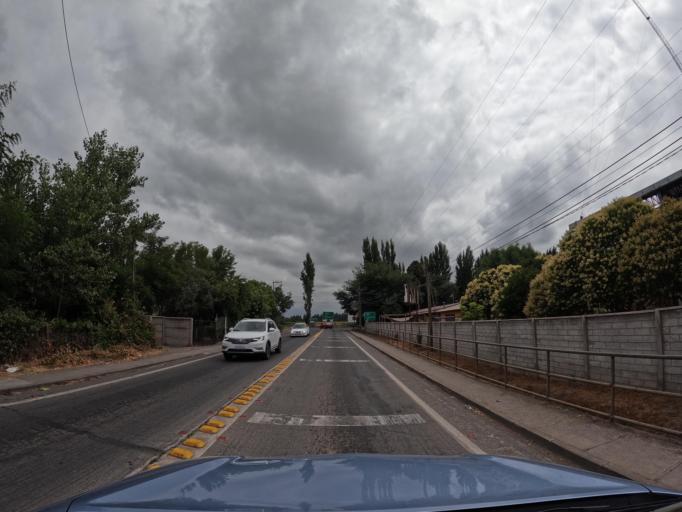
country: CL
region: Maule
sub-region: Provincia de Curico
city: Teno
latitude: -34.7500
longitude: -71.2383
